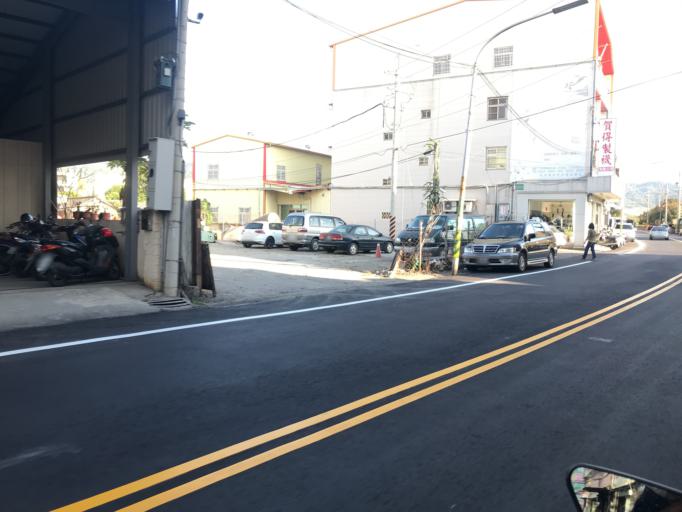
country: TW
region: Taiwan
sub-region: Nantou
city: Nantou
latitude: 23.8982
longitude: 120.5925
